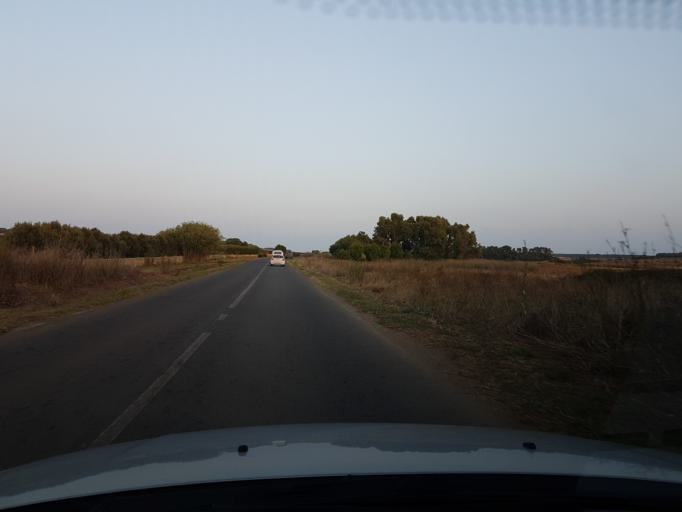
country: IT
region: Sardinia
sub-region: Provincia di Oristano
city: Cabras
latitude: 39.9463
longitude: 8.4322
